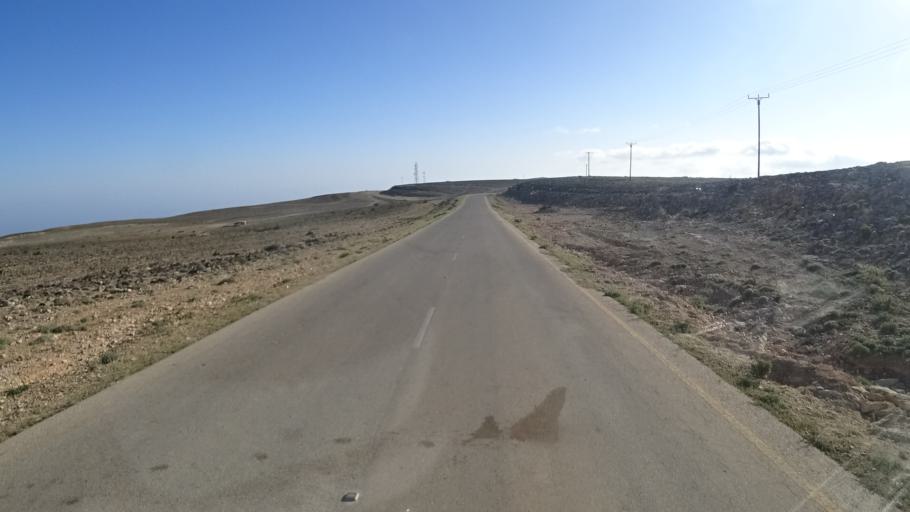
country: OM
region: Zufar
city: Salalah
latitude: 17.1113
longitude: 54.7015
